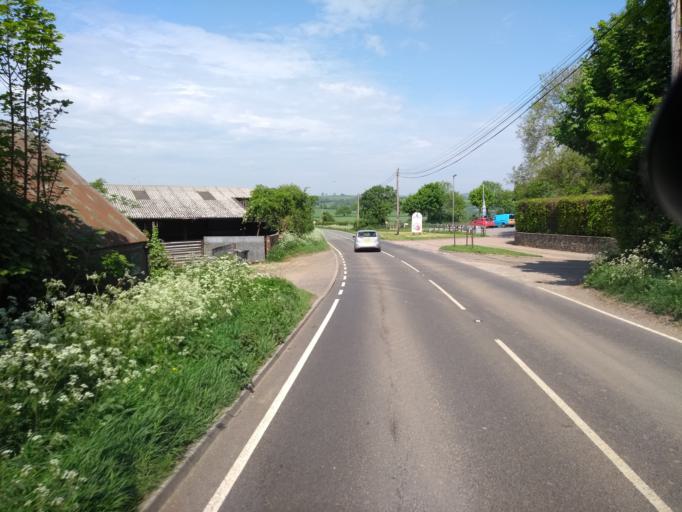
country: GB
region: England
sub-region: Somerset
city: Chard
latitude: 50.8771
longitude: -2.9877
